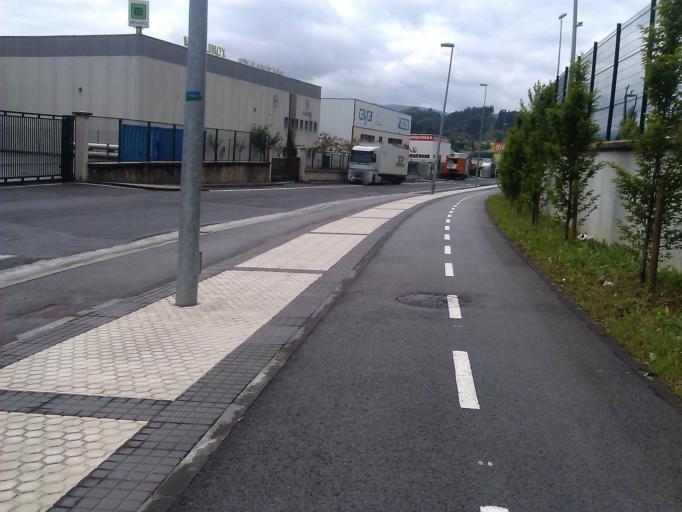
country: ES
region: Basque Country
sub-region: Provincia de Guipuzcoa
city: Urnieta
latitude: 43.2317
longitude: -2.0009
